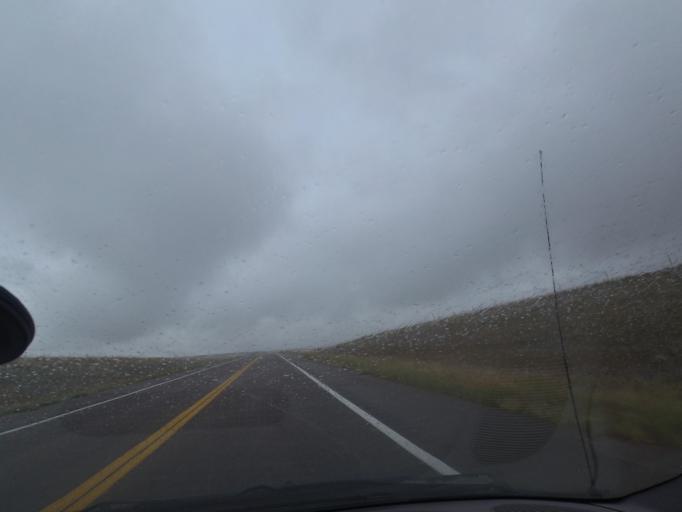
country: US
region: Colorado
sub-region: Arapahoe County
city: Byers
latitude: 39.7333
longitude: -103.9016
